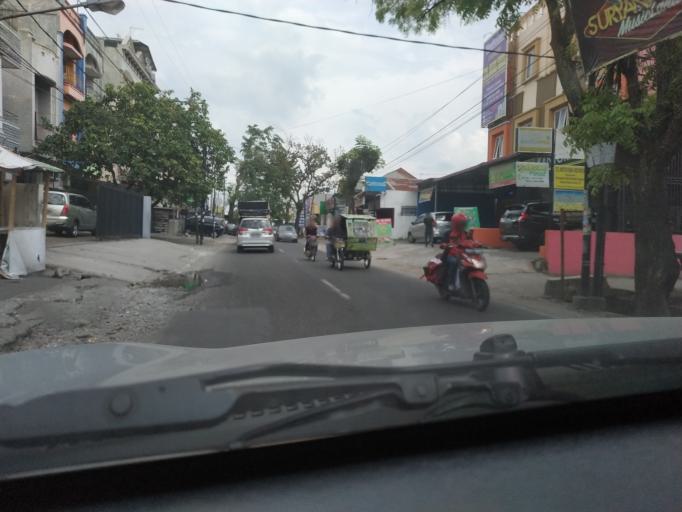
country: ID
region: North Sumatra
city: Sunggal
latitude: 3.5843
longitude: 98.6385
